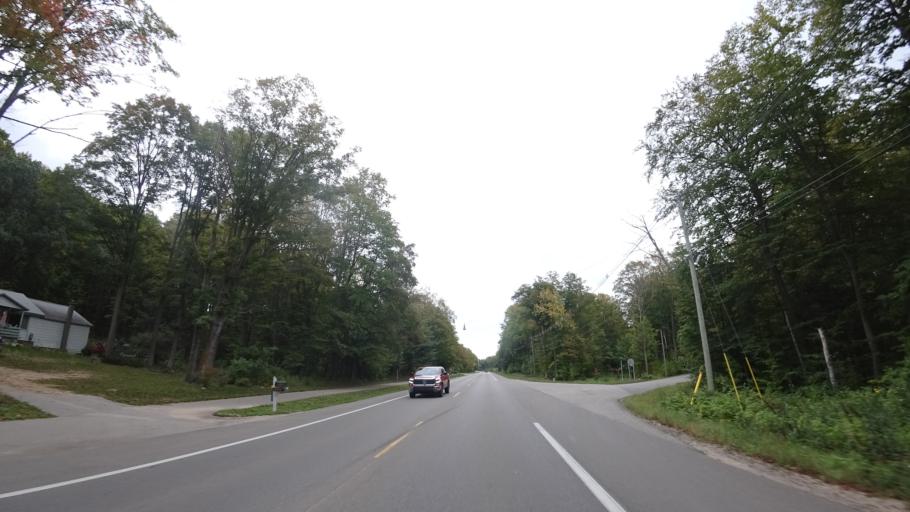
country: US
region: Michigan
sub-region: Emmet County
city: Petoskey
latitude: 45.4294
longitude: -84.9246
